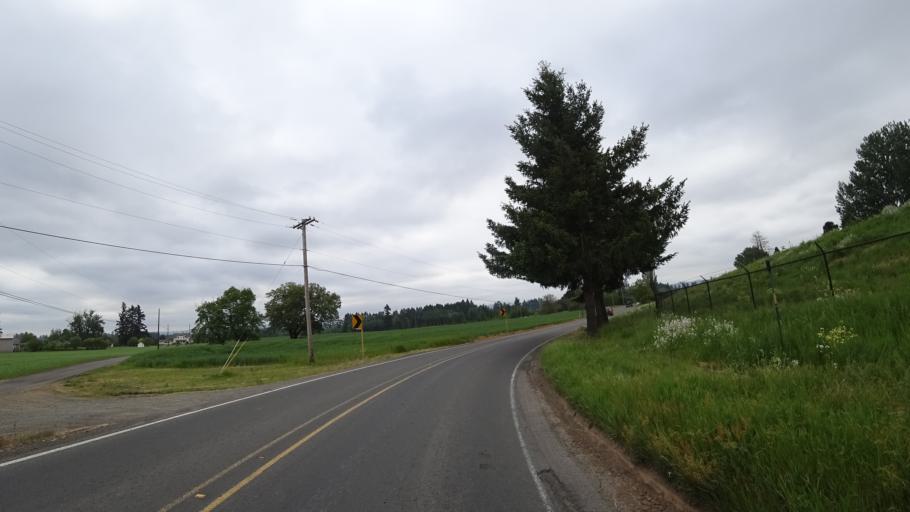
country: US
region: Oregon
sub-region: Washington County
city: Hillsboro
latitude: 45.4892
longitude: -122.9704
